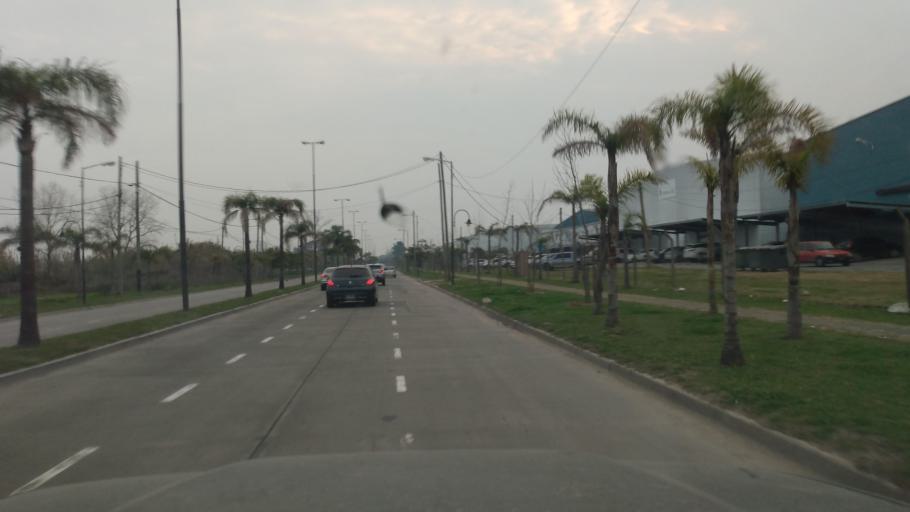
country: AR
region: Buenos Aires
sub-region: Partido de Tigre
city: Tigre
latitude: -34.4582
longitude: -58.5879
